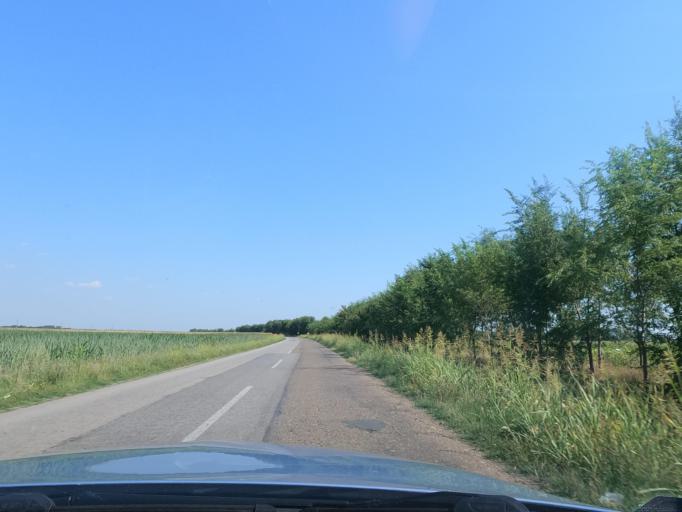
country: RS
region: Autonomna Pokrajina Vojvodina
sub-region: Juznobacki Okrug
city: Becej
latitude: 45.6548
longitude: 19.9639
